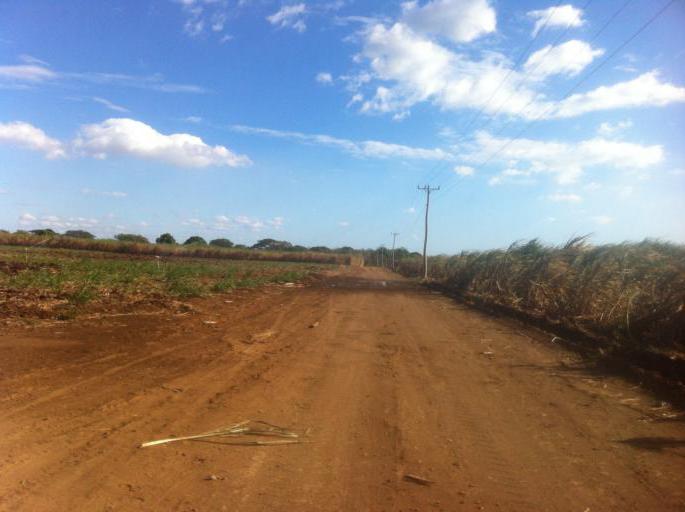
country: NI
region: Managua
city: Carlos Fonseca Amador
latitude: 11.9036
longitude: -86.5898
